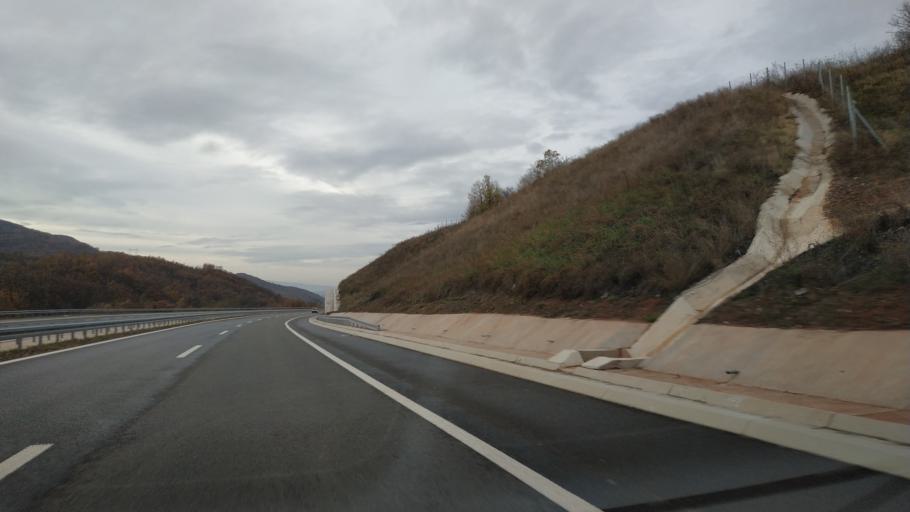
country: RS
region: Central Serbia
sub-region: Nisavski Okrug
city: Gadzin Han
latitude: 43.2821
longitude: 22.1286
